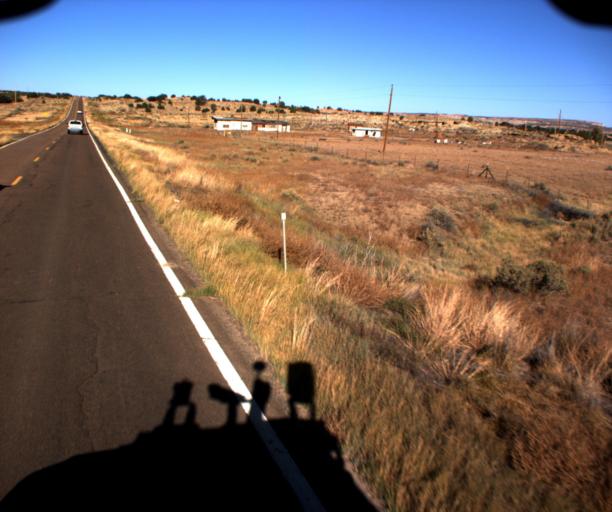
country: US
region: Arizona
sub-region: Apache County
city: Ganado
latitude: 35.7499
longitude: -109.8791
